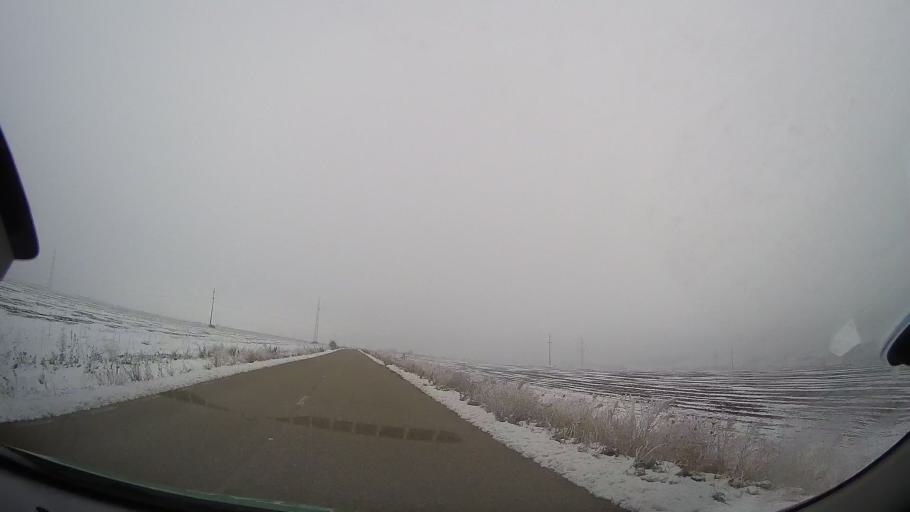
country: RO
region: Vaslui
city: Coroiesti
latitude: 46.2331
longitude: 27.4777
